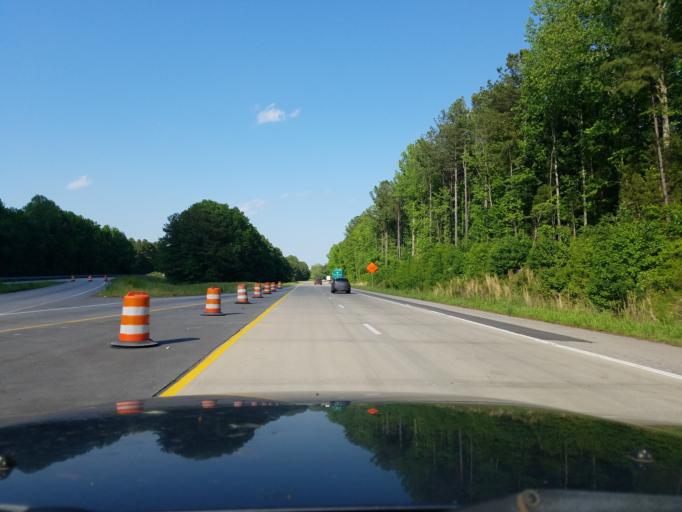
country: US
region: North Carolina
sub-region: Vance County
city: Henderson
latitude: 36.3354
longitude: -78.4350
